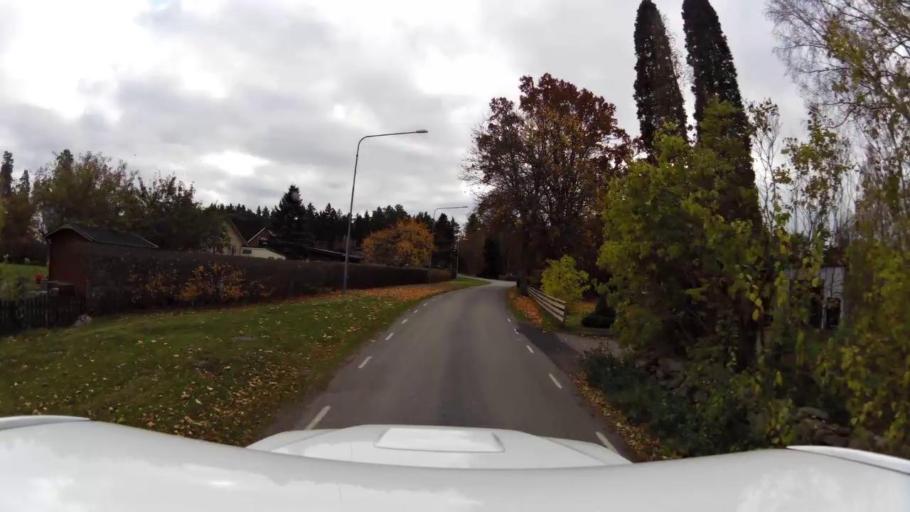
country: SE
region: OEstergoetland
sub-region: Linkopings Kommun
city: Linghem
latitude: 58.4056
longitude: 15.8452
